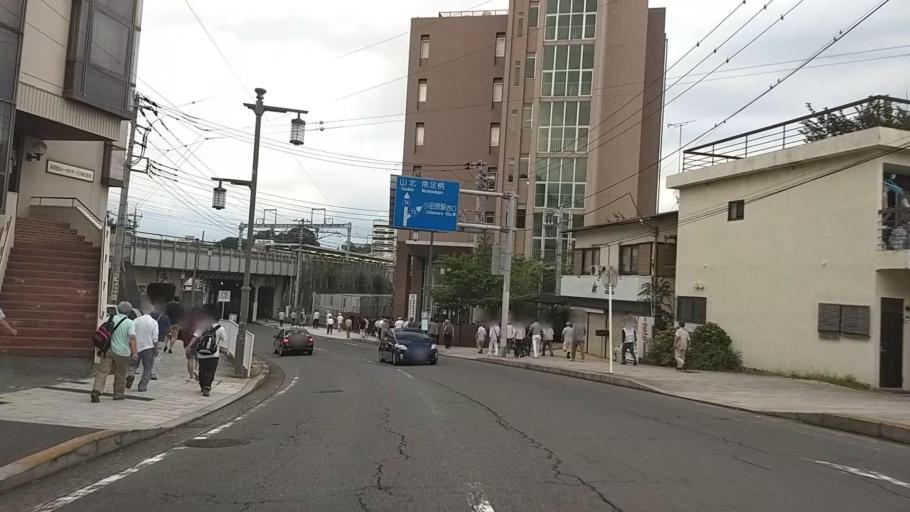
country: JP
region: Kanagawa
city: Odawara
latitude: 35.2536
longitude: 139.1532
